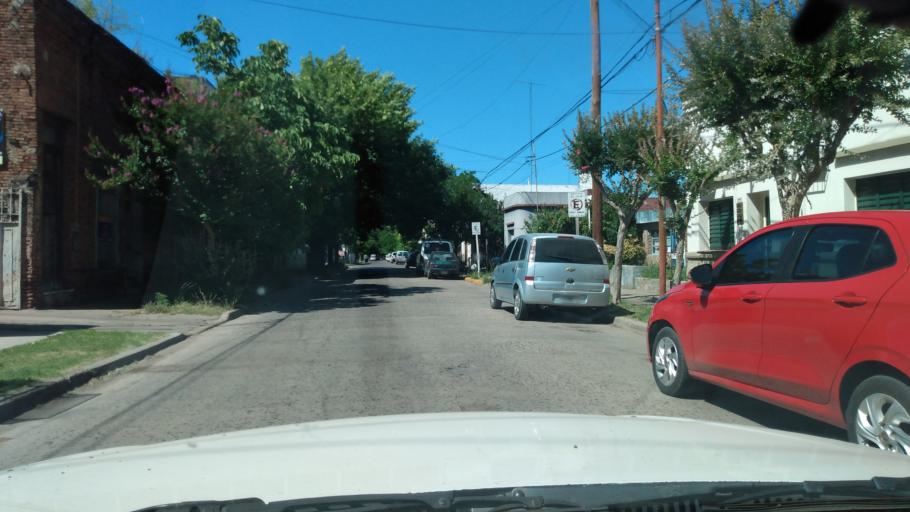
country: AR
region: Buenos Aires
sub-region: Partido de Lujan
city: Lujan
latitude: -34.5690
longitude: -59.1102
